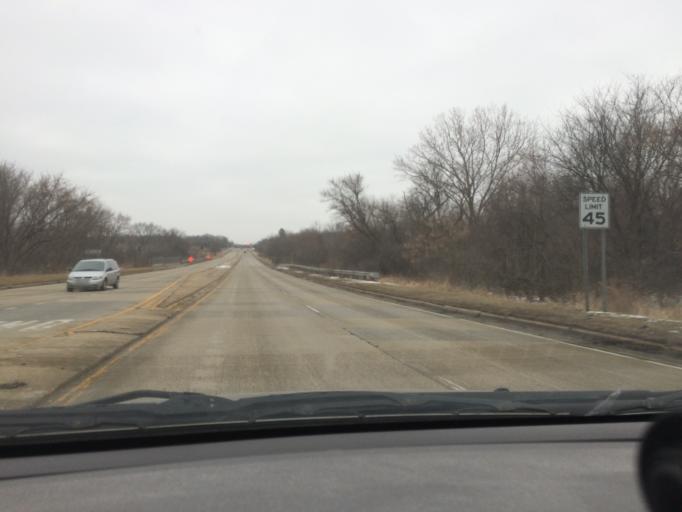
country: US
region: Illinois
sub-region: Cook County
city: Streamwood
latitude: 42.0459
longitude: -88.1791
